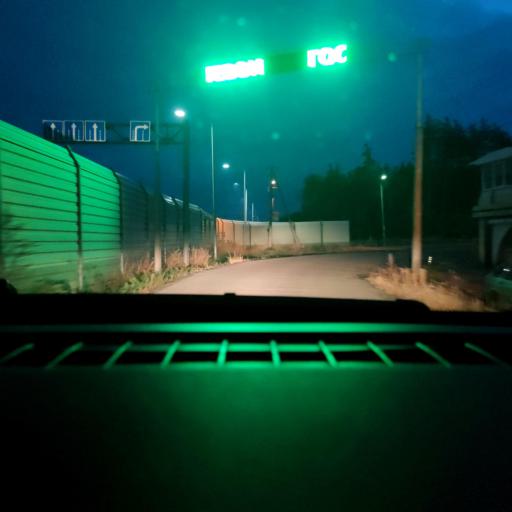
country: RU
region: Voronezj
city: Somovo
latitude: 51.6874
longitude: 39.3029
